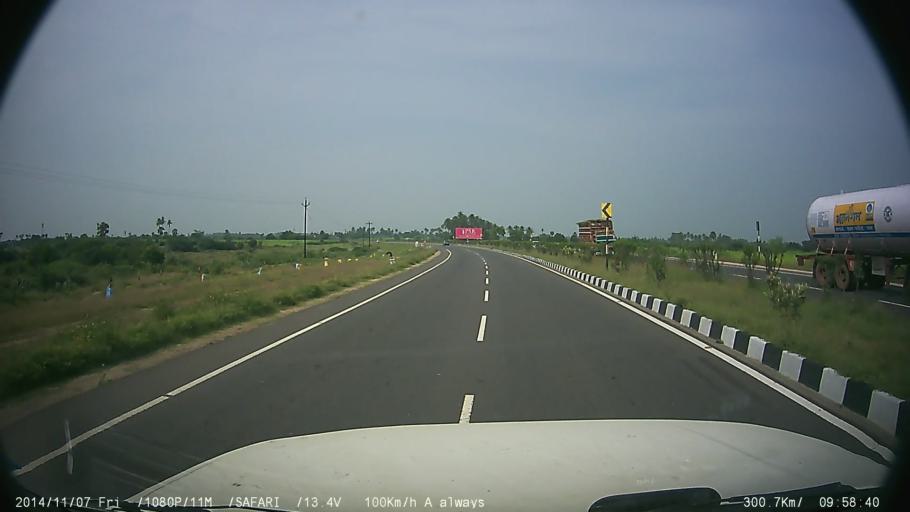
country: IN
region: Tamil Nadu
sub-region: Tiruppur
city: Uttukkuli
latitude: 11.2183
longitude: 77.4504
